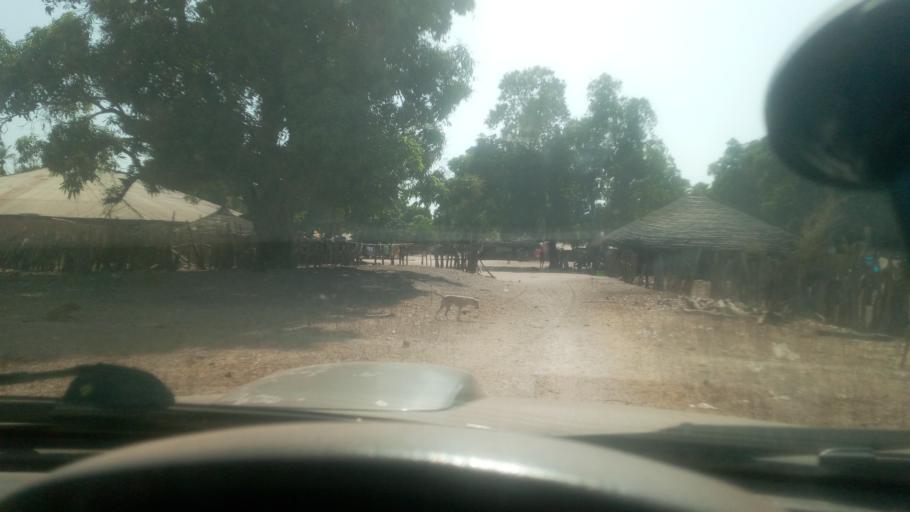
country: GW
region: Oio
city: Farim
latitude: 12.4524
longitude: -15.4225
